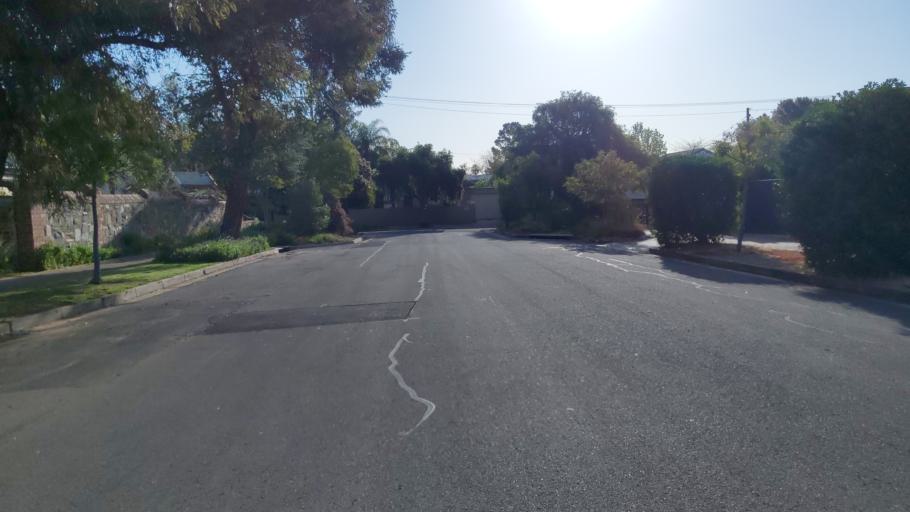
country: AU
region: South Australia
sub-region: Unley
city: Fullarton
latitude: -34.9516
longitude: 138.6293
